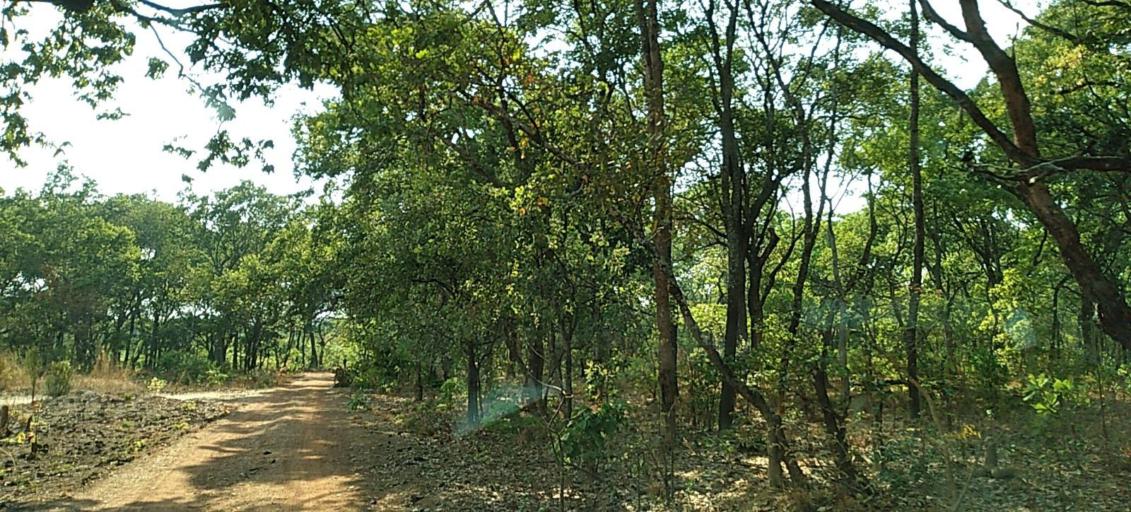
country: ZM
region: Copperbelt
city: Kalulushi
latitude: -13.0062
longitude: 27.7343
